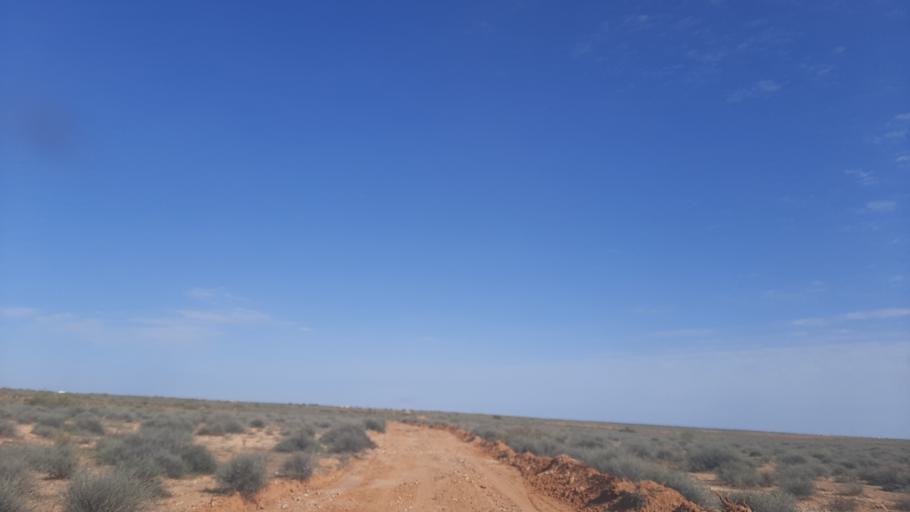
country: TN
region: Madanin
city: Medenine
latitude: 33.2459
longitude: 10.7441
